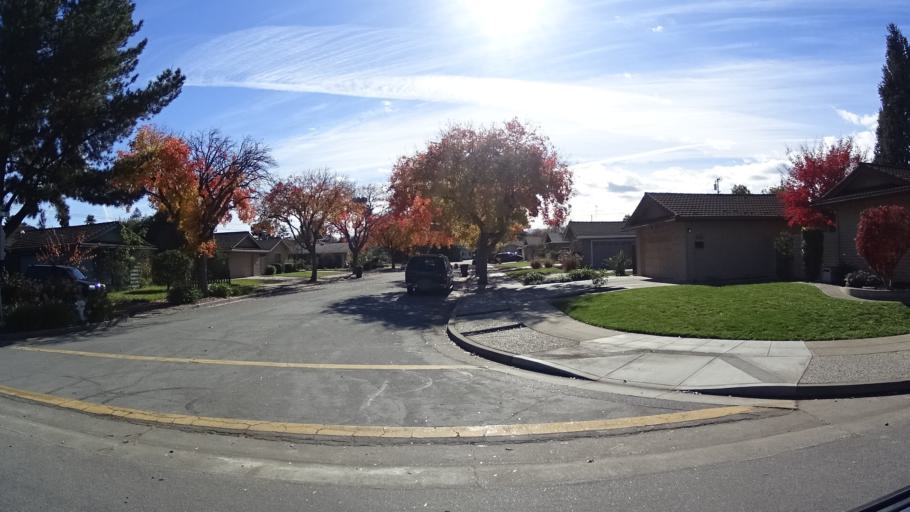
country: US
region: California
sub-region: Santa Clara County
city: Sunnyvale
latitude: 37.3467
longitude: -122.0398
